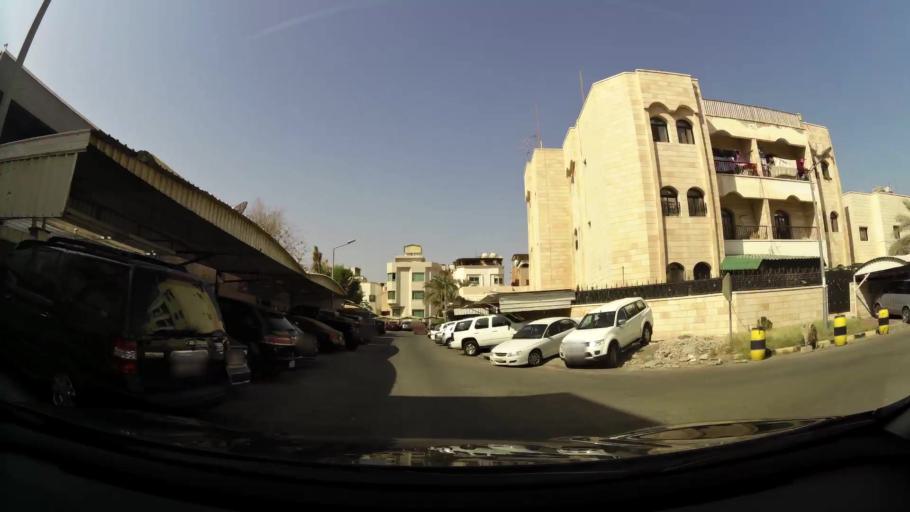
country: KW
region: Muhafazat Hawalli
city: Salwa
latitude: 29.2813
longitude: 48.0799
